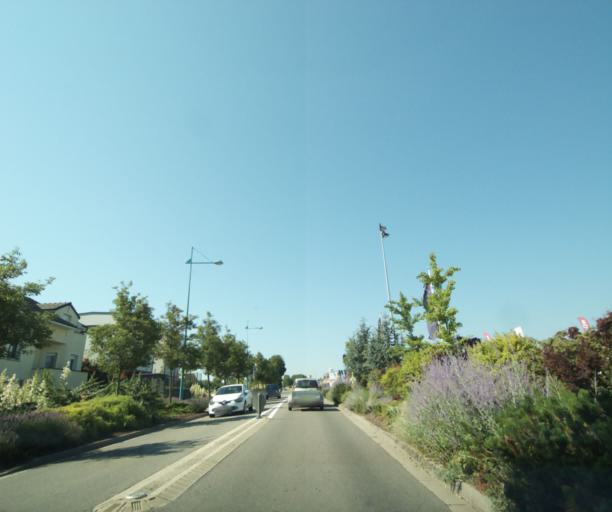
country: FR
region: Lorraine
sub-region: Departement de Meurthe-et-Moselle
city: Toul
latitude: 48.6639
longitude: 5.8797
